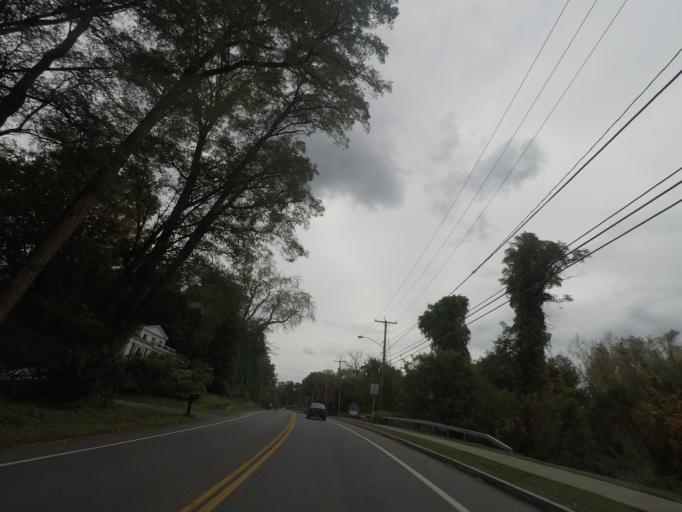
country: US
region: New York
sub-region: Albany County
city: McKownville
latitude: 42.6638
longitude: -73.8445
